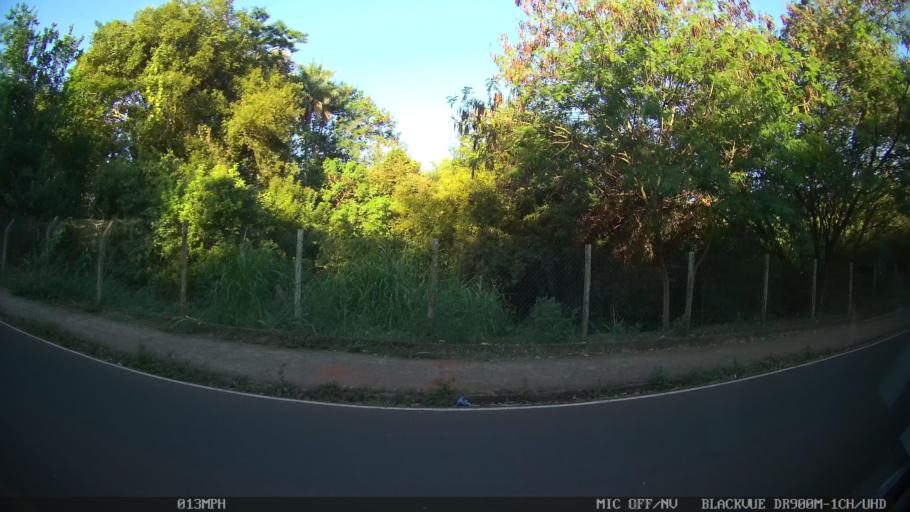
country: BR
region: Sao Paulo
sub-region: Sao Jose Do Rio Preto
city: Sao Jose do Rio Preto
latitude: -20.7740
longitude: -49.3550
